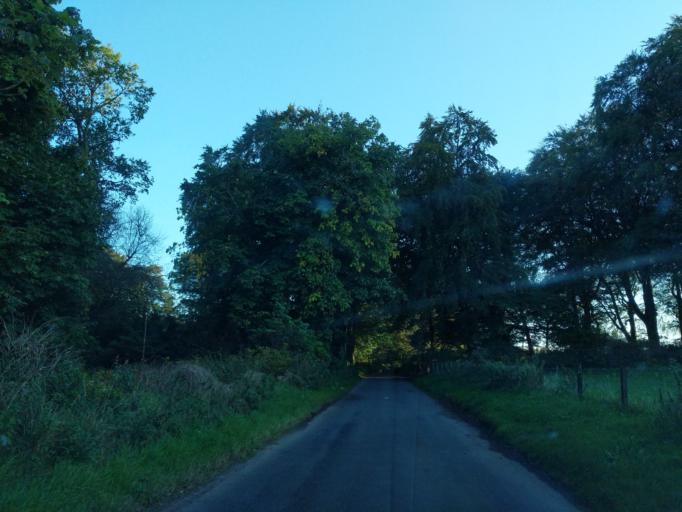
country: GB
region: Scotland
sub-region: The Scottish Borders
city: West Linton
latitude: 55.7066
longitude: -3.4356
